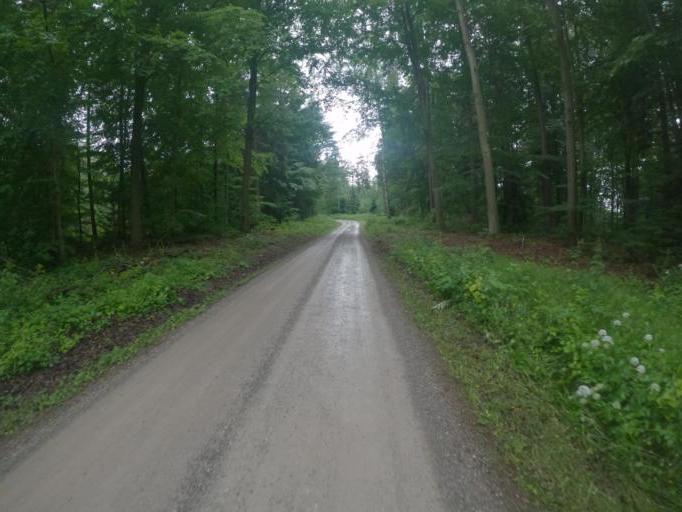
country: DE
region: Baden-Wuerttemberg
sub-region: Regierungsbezirk Stuttgart
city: Schorndorf
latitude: 48.7690
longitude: 9.5388
